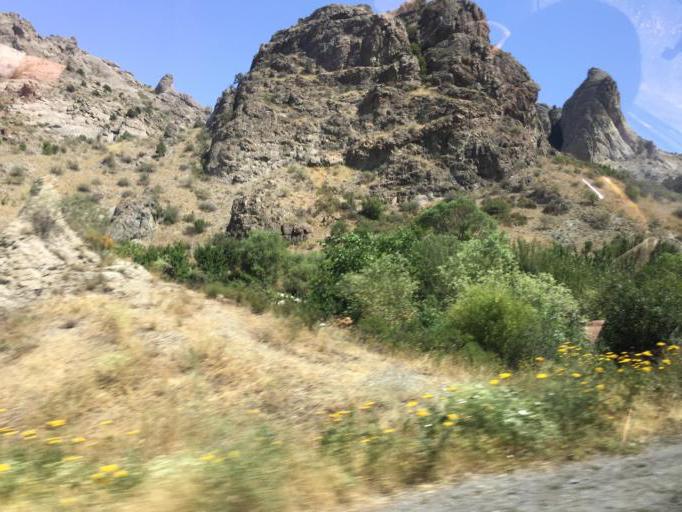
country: AM
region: Vayots' Dzori Marz
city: Zarrit'ap'
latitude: 39.7001
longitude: 45.5947
